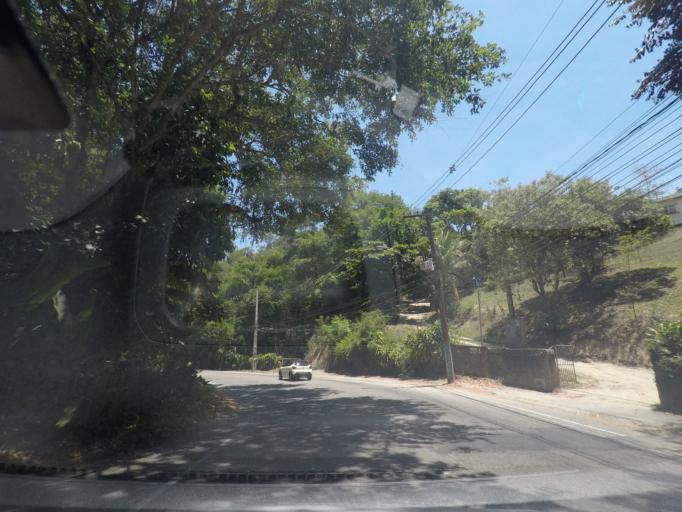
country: BR
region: Rio de Janeiro
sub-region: Niteroi
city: Niteroi
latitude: -22.9233
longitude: -43.0667
